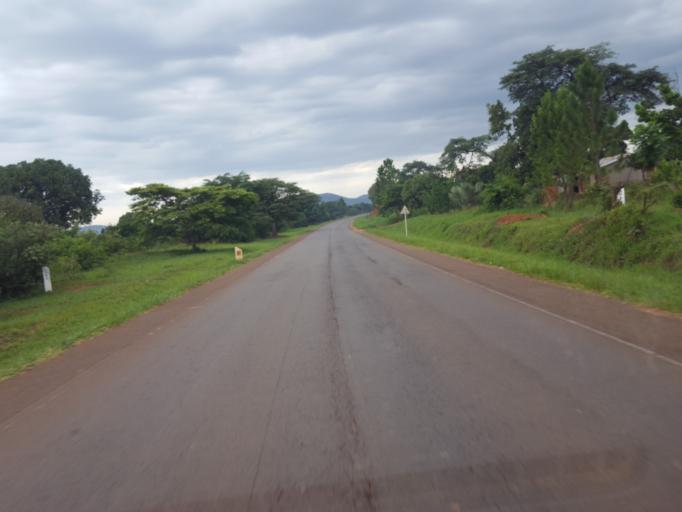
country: UG
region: Central Region
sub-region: Kiboga District
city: Kiboga
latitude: 0.8774
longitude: 31.8463
